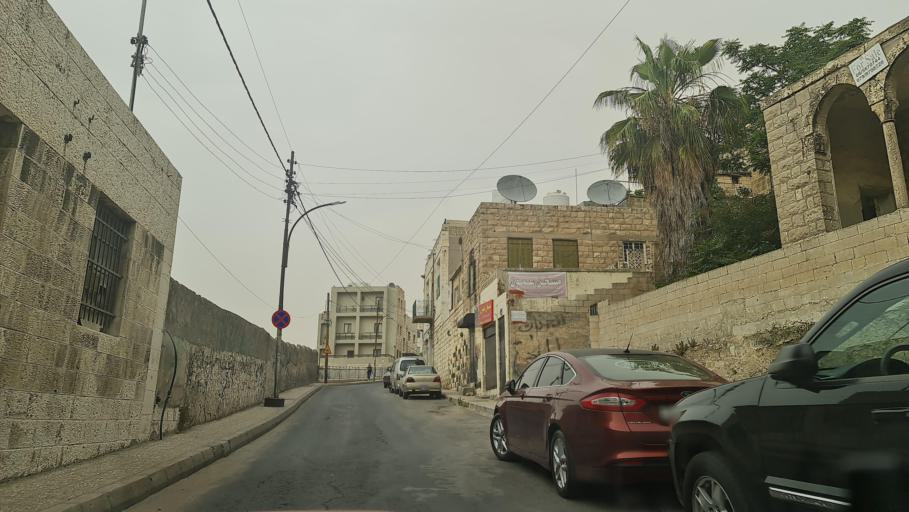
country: JO
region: Amman
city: Amman
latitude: 31.9511
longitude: 35.9287
